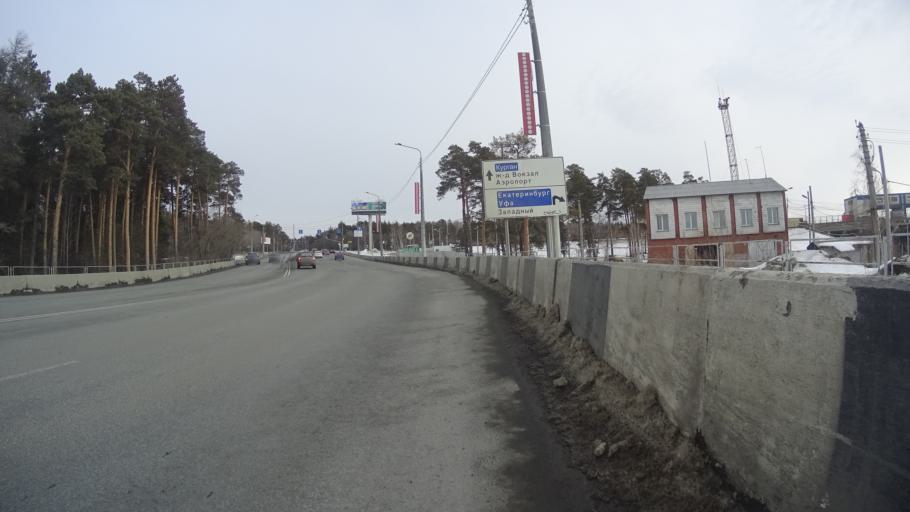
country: RU
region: Chelyabinsk
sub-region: Gorod Chelyabinsk
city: Chelyabinsk
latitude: 55.1477
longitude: 61.3270
